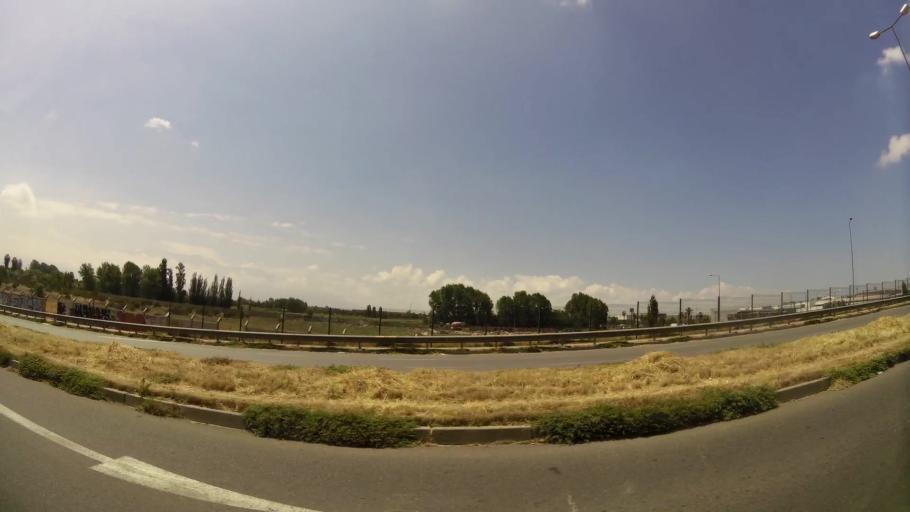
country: CL
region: Santiago Metropolitan
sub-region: Provincia de Santiago
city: Lo Prado
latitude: -33.5130
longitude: -70.7178
